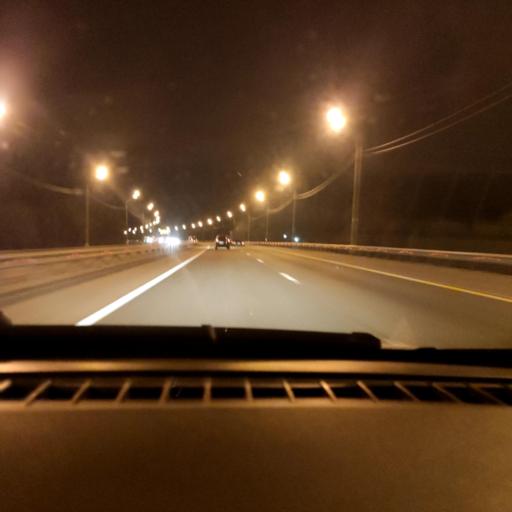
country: RU
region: Lipetsk
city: Khlevnoye
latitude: 52.2501
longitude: 39.0661
